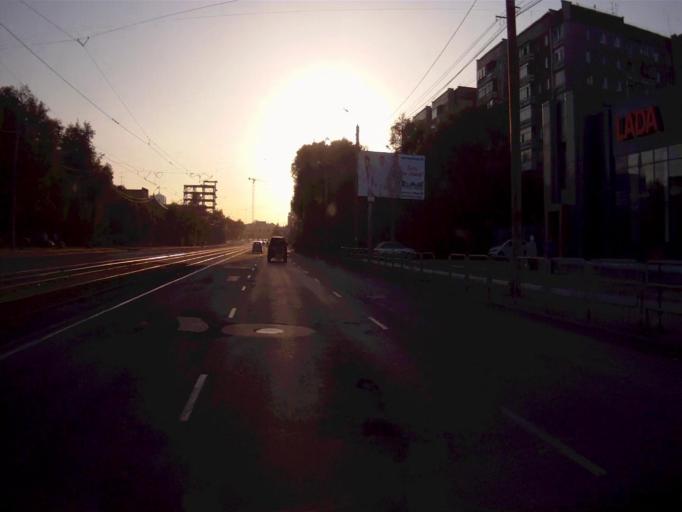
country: RU
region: Chelyabinsk
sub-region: Gorod Chelyabinsk
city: Chelyabinsk
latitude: 55.1682
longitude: 61.4271
